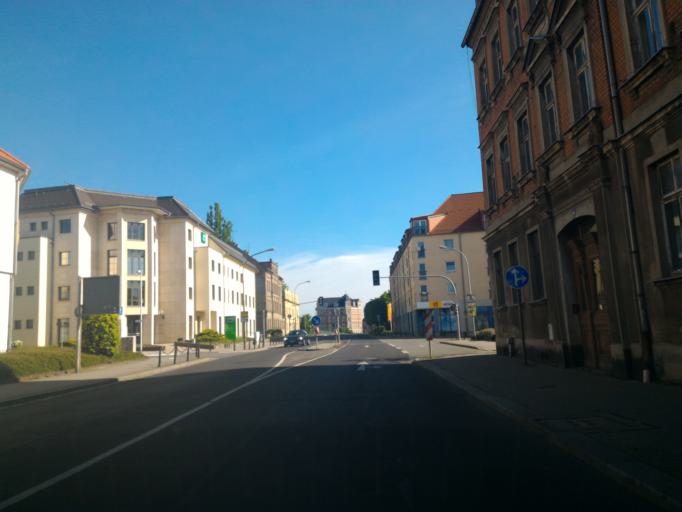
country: DE
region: Saxony
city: Lobau
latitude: 51.0985
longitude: 14.6663
